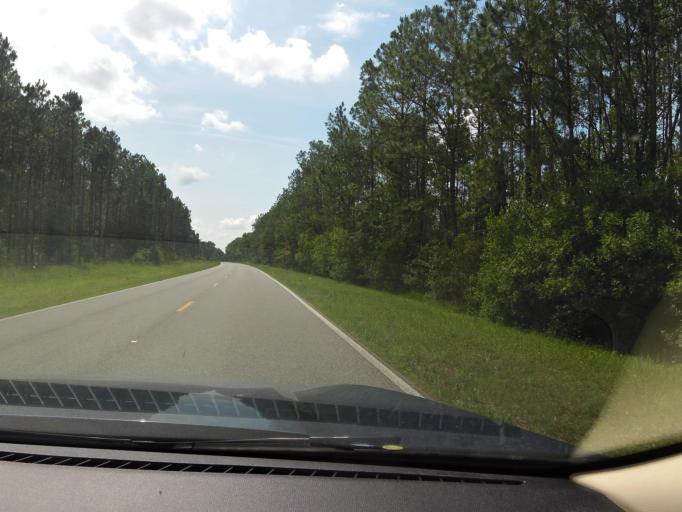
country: US
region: Florida
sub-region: Baker County
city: Macclenny
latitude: 30.2591
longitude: -82.0951
